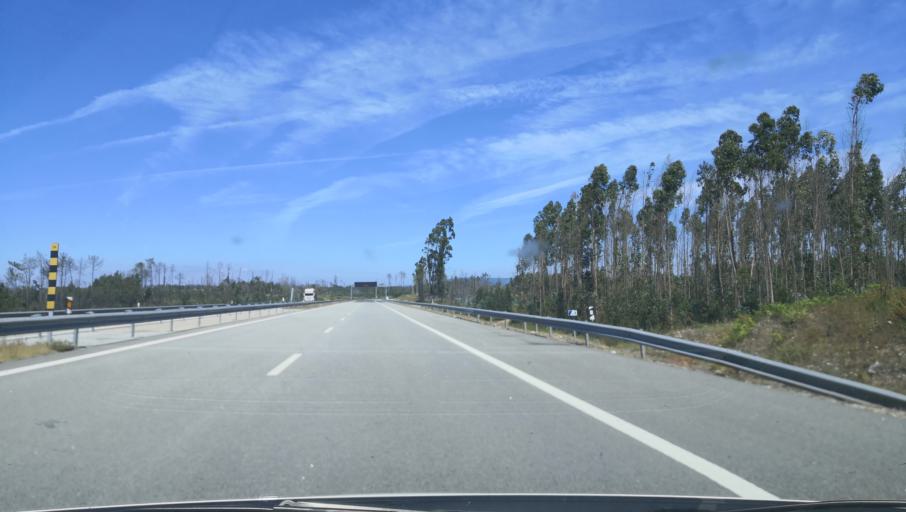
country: PT
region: Coimbra
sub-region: Cantanhede
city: Cantanhede
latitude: 40.2819
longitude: -8.5814
